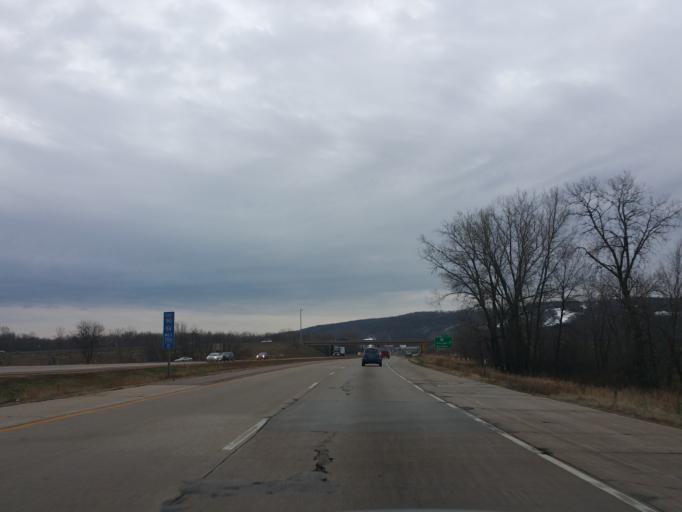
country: US
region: Wisconsin
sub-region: Columbia County
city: Portage
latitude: 43.5157
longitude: -89.5255
